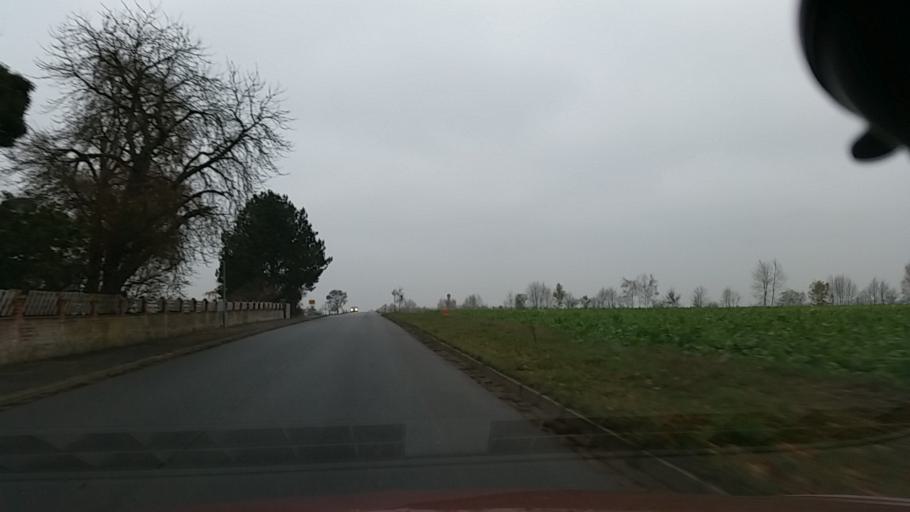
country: DE
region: Lower Saxony
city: Uelzen
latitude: 52.9409
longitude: 10.5772
